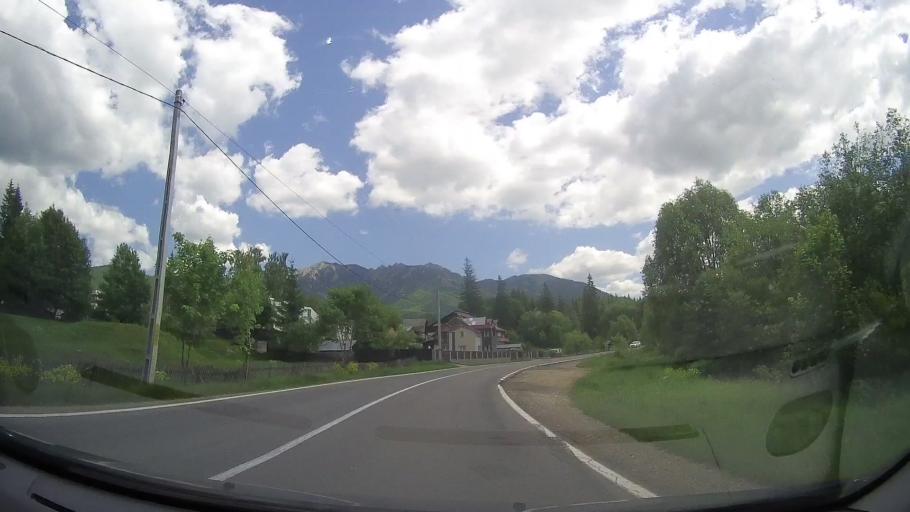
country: RO
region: Brasov
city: Crivina
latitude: 45.4545
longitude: 25.9374
